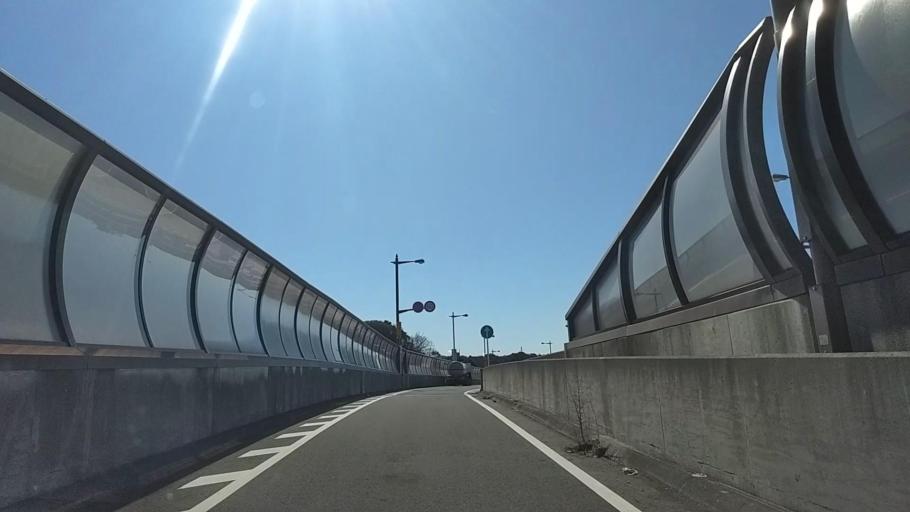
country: JP
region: Kanagawa
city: Fujisawa
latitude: 35.3389
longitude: 139.5027
